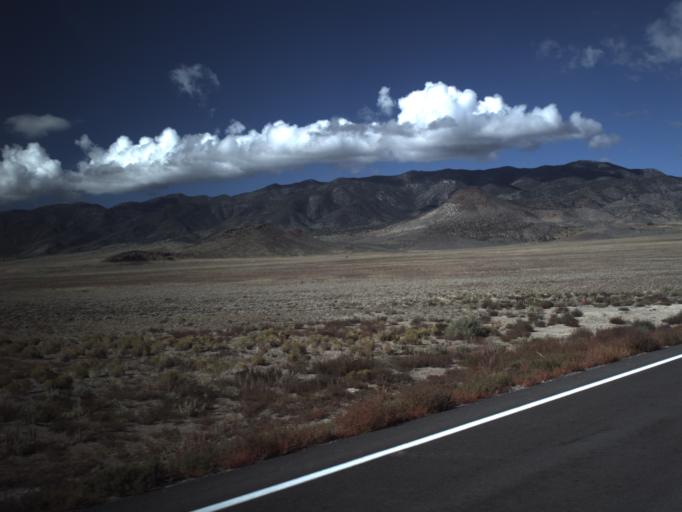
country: US
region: Utah
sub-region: Beaver County
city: Milford
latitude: 38.4791
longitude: -113.4335
